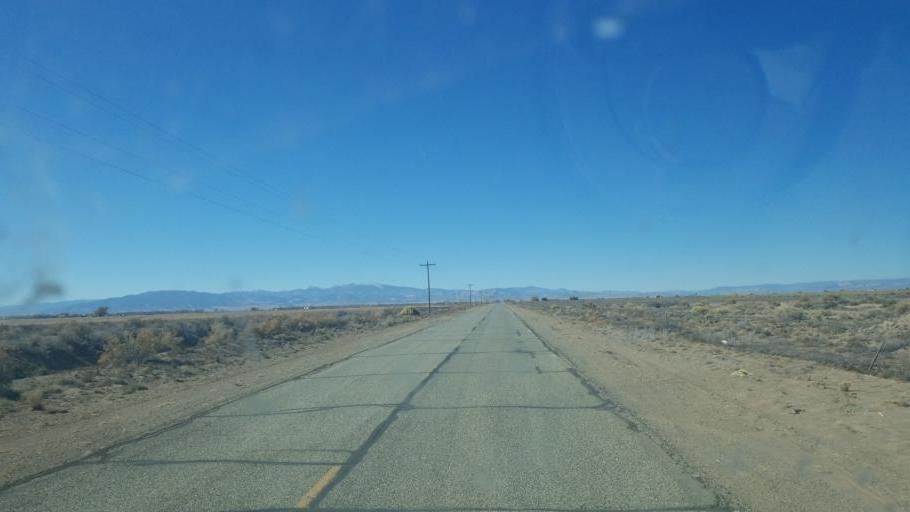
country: US
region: Colorado
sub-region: Alamosa County
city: Alamosa
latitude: 37.5745
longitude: -105.9199
